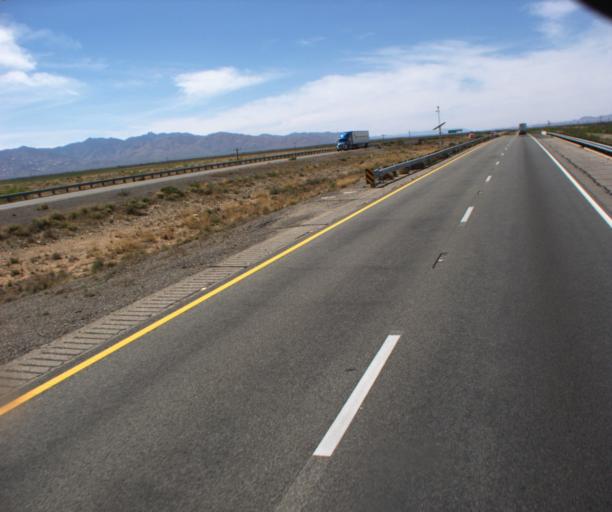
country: US
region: Arizona
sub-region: Cochise County
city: Willcox
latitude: 32.2968
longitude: -109.3511
